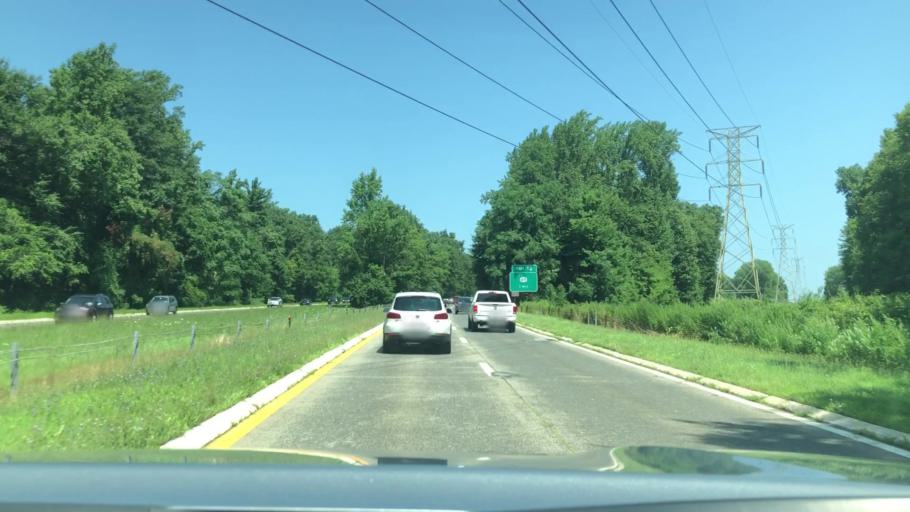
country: US
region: New York
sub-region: Rockland County
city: New Hempstead
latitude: 41.1526
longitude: -74.0262
